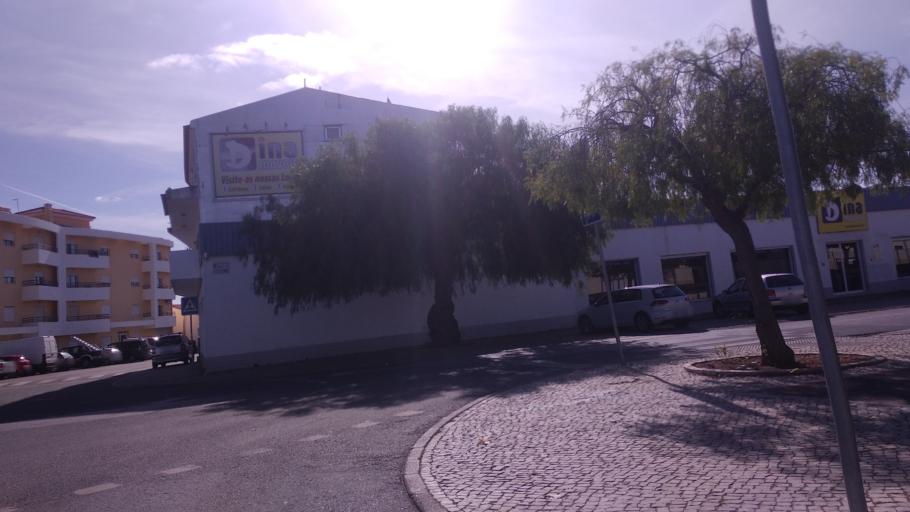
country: PT
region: Faro
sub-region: Sao Bras de Alportel
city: Sao Bras de Alportel
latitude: 37.1570
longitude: -7.8854
